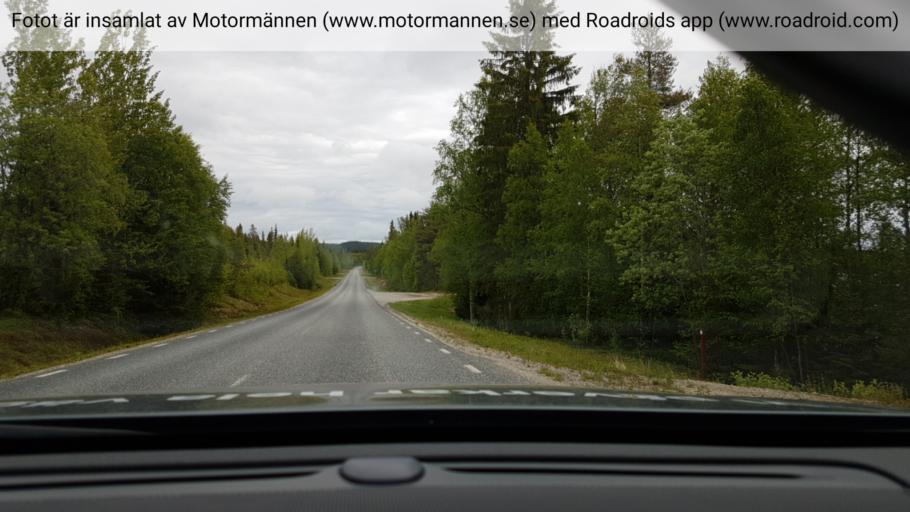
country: SE
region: Vaesterbotten
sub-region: Asele Kommun
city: Insjon
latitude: 64.3359
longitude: 17.7547
